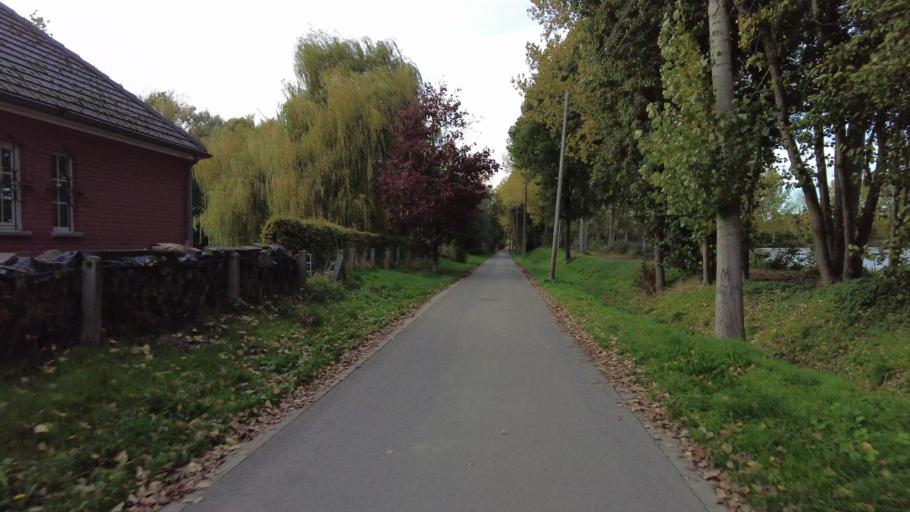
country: BE
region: Flanders
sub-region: Provincie Vlaams-Brabant
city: Hoegaarden
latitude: 50.7625
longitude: 4.8938
